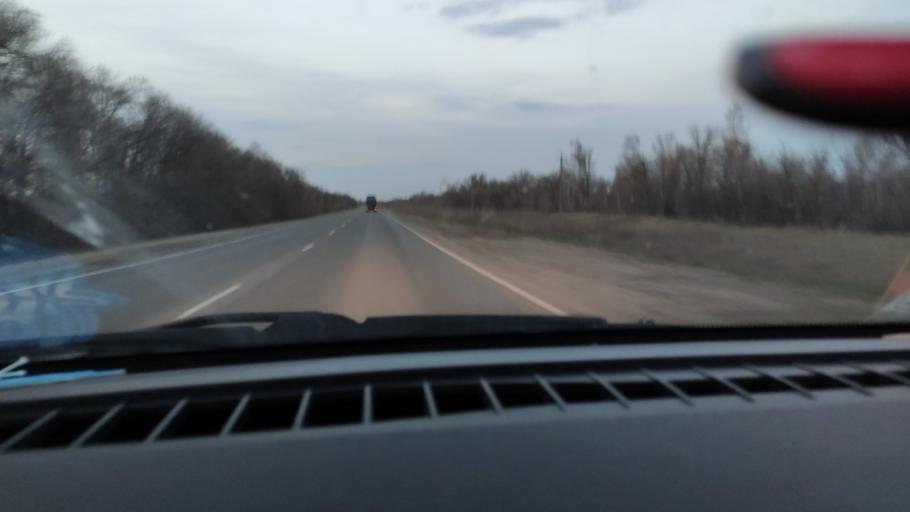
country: RU
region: Saratov
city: Sinodskoye
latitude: 52.0316
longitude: 46.7233
